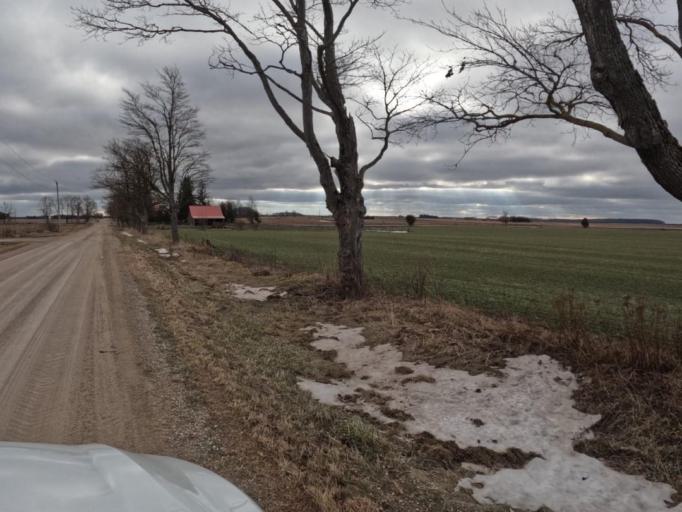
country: CA
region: Ontario
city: Shelburne
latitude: 43.8829
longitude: -80.4048
